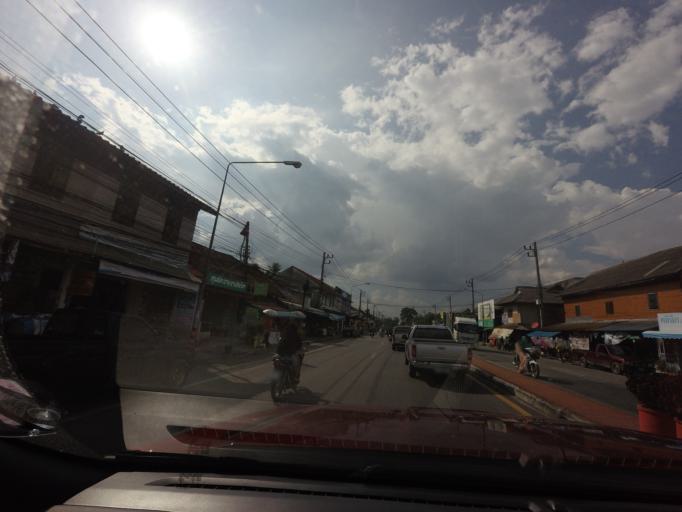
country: TH
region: Pattani
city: Mae Lan
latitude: 6.5797
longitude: 101.1982
